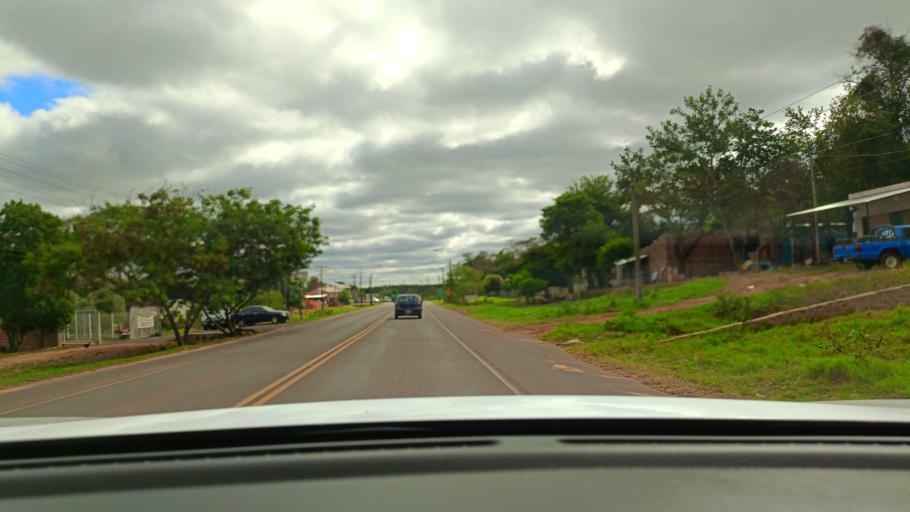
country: PY
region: San Pedro
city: Guayaybi
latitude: -24.6587
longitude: -56.4598
